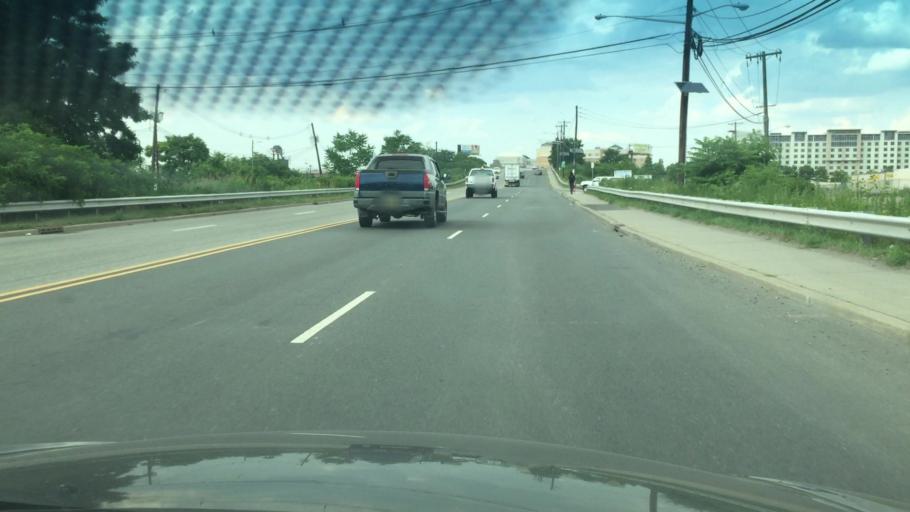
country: US
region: New Jersey
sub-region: Union County
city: Elizabeth
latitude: 40.6586
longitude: -74.1813
